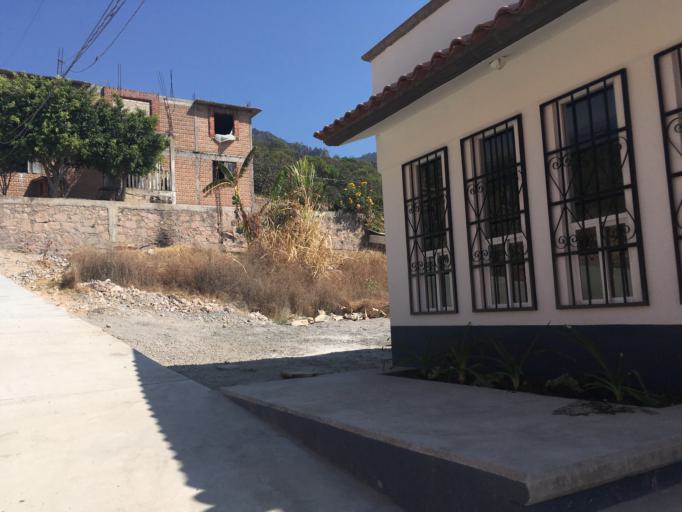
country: MX
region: Guerrero
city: Taxco de Alarcon
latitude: 18.5784
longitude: -99.6029
